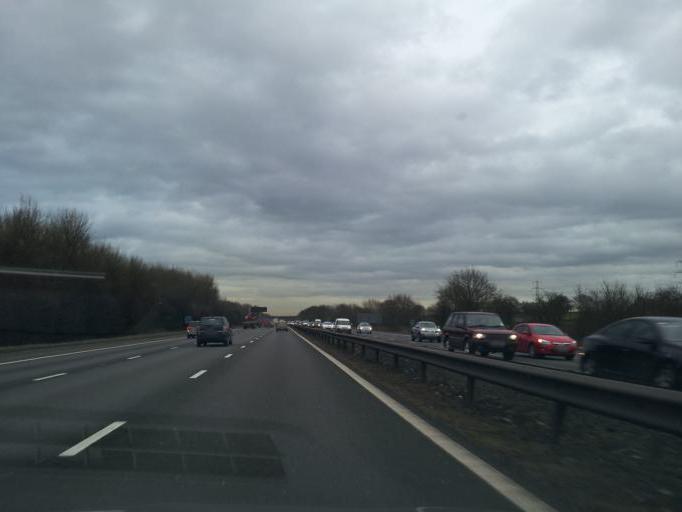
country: GB
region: England
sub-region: Coventry
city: Keresley
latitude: 52.4704
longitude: -1.5359
